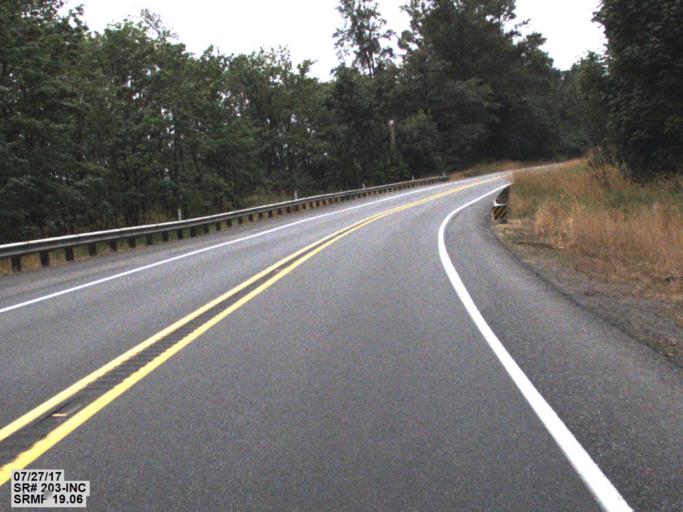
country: US
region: Washington
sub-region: King County
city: Duvall
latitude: 47.7887
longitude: -121.9741
